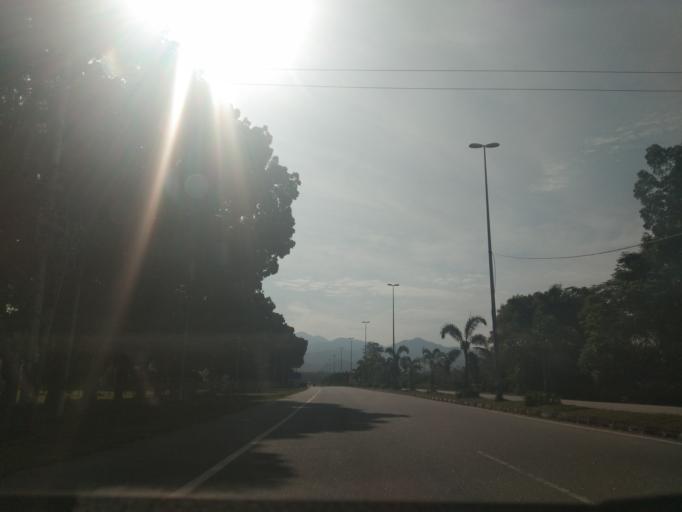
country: MY
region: Perak
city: Ipoh
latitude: 4.5012
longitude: 101.1409
